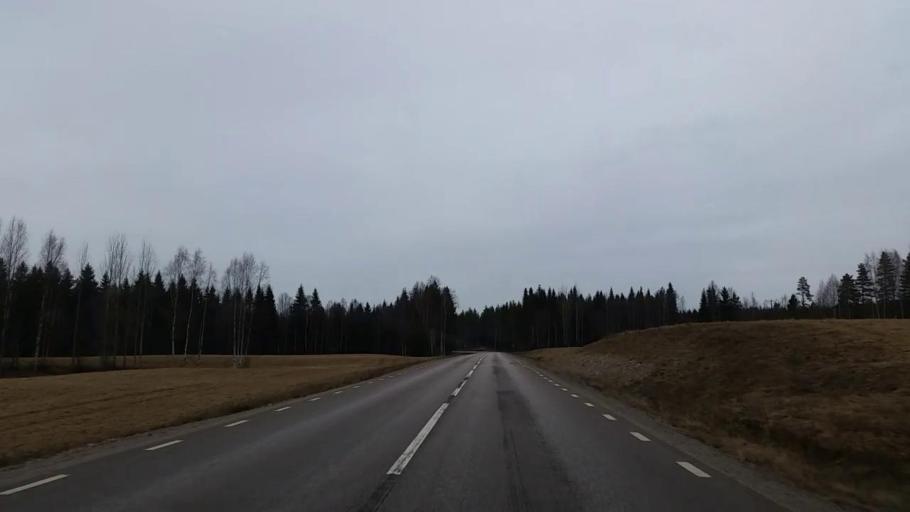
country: SE
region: Gaevleborg
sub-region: Ovanakers Kommun
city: Edsbyn
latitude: 61.1987
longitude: 15.8738
